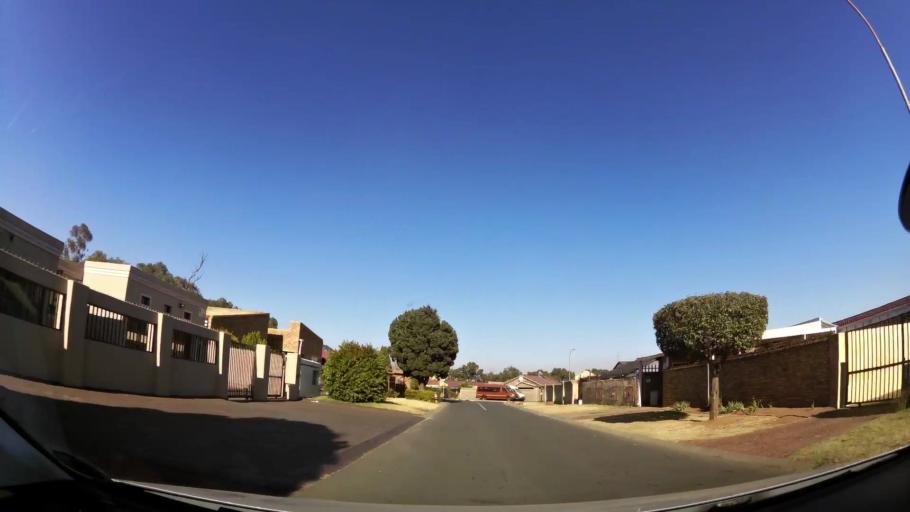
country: ZA
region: Gauteng
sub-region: City of Johannesburg Metropolitan Municipality
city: Johannesburg
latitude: -26.2072
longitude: 27.9643
